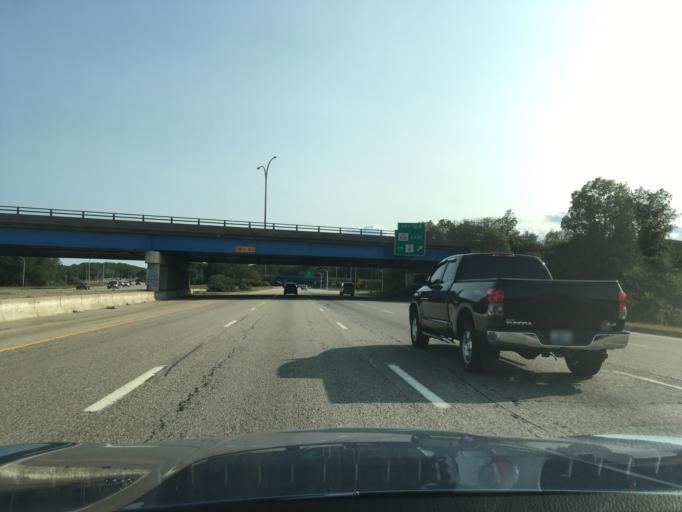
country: US
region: Rhode Island
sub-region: Kent County
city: West Warwick
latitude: 41.7168
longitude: -71.4709
